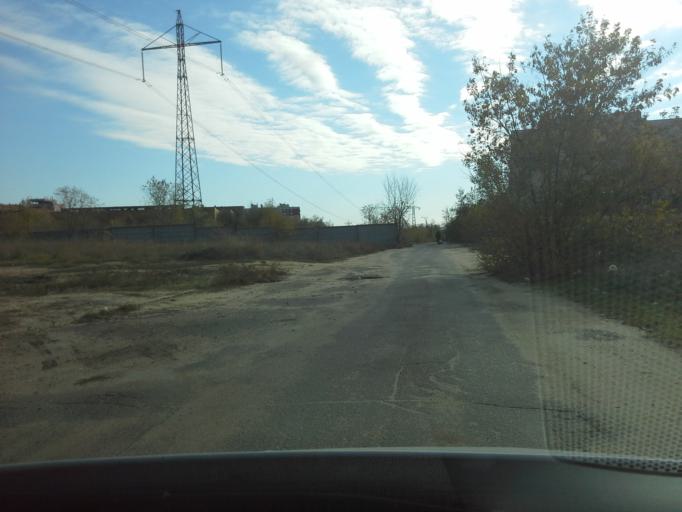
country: RU
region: Volgograd
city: Vodstroy
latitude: 48.8376
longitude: 44.6299
